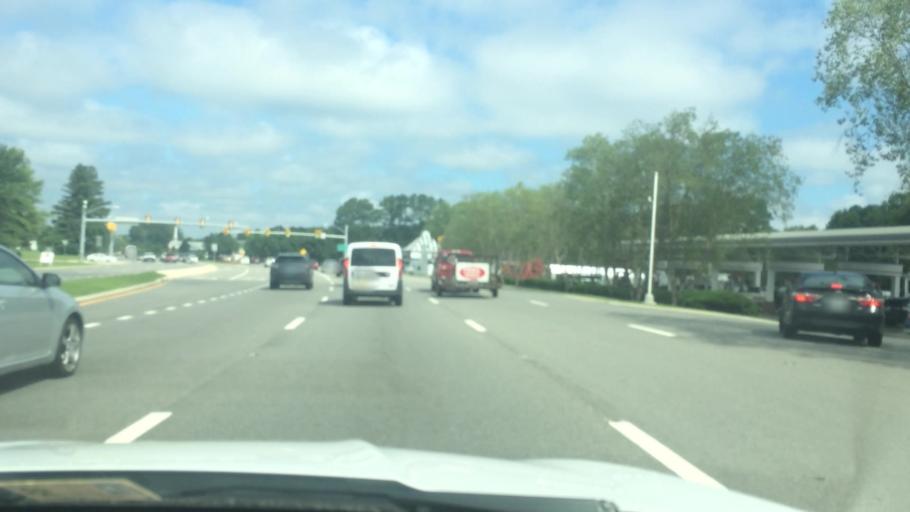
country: US
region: Virginia
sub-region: York County
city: Yorktown
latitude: 37.1646
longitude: -76.4653
